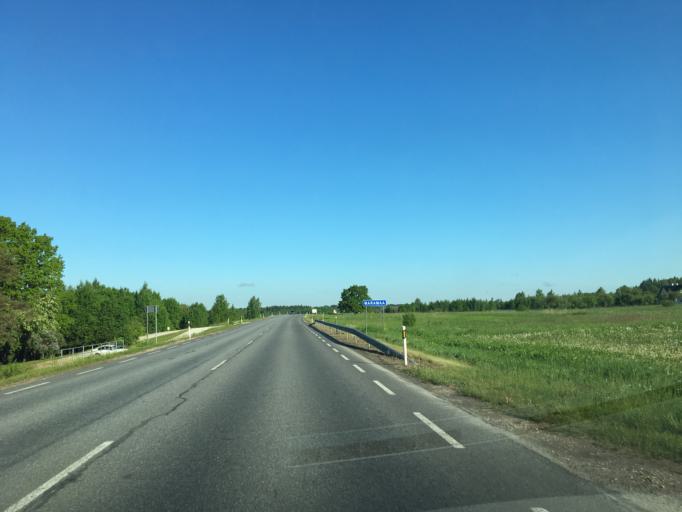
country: EE
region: Tartu
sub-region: Tartu linn
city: Tartu
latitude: 58.4282
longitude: 26.6872
